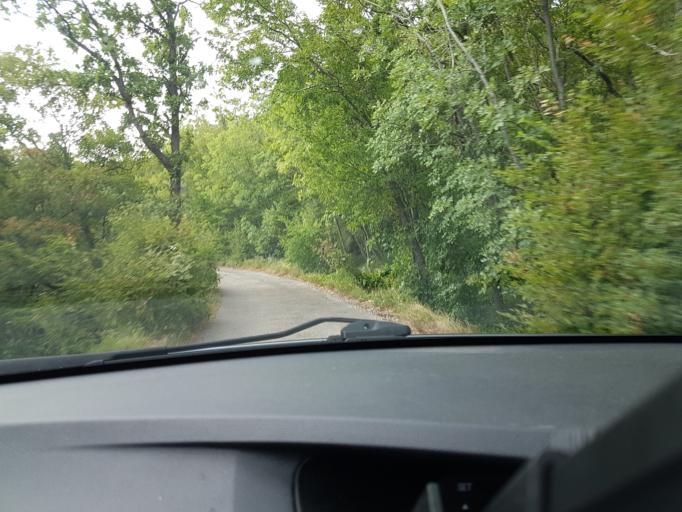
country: HR
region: Primorsko-Goranska
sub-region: Grad Crikvenica
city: Crikvenica
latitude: 45.2279
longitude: 14.7074
